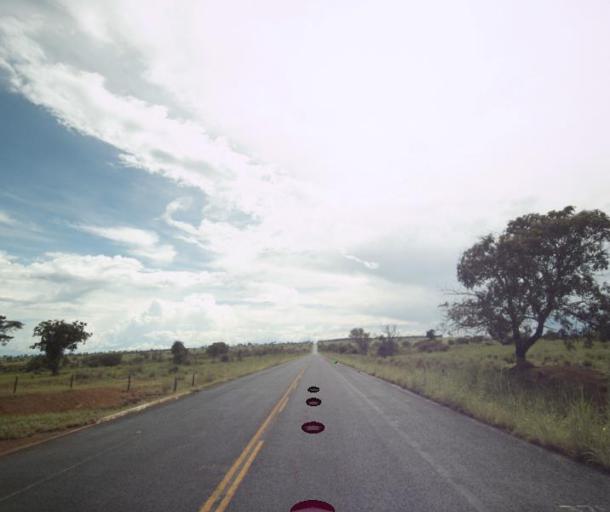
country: BR
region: Goias
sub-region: Sao Miguel Do Araguaia
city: Sao Miguel do Araguaia
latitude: -13.3019
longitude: -50.2816
